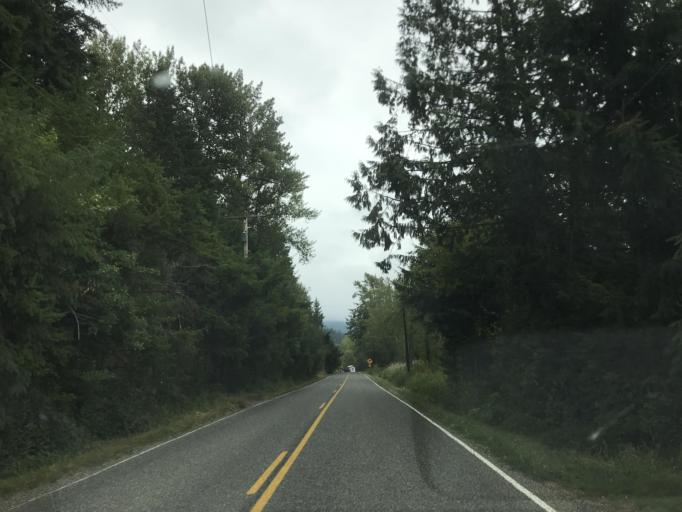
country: US
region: Washington
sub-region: Whatcom County
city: Sudden Valley
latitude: 48.8004
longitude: -122.3351
